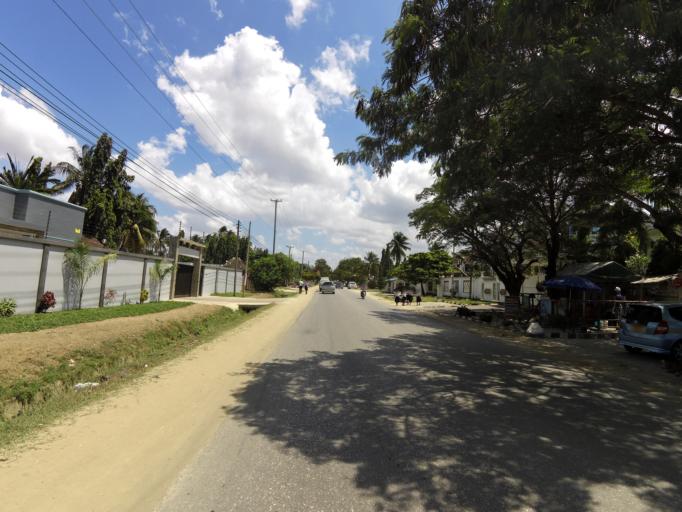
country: TZ
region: Dar es Salaam
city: Magomeni
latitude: -6.7637
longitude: 39.2496
